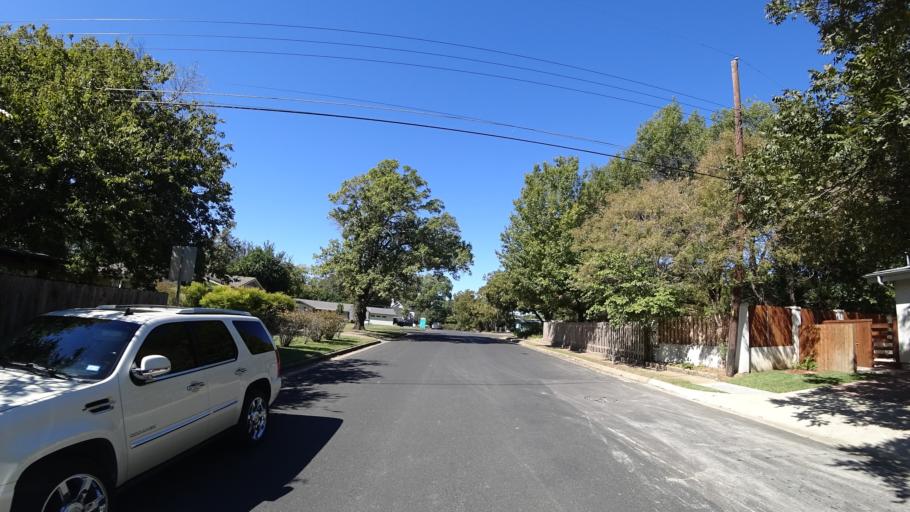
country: US
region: Texas
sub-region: Travis County
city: West Lake Hills
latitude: 30.3382
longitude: -97.7446
